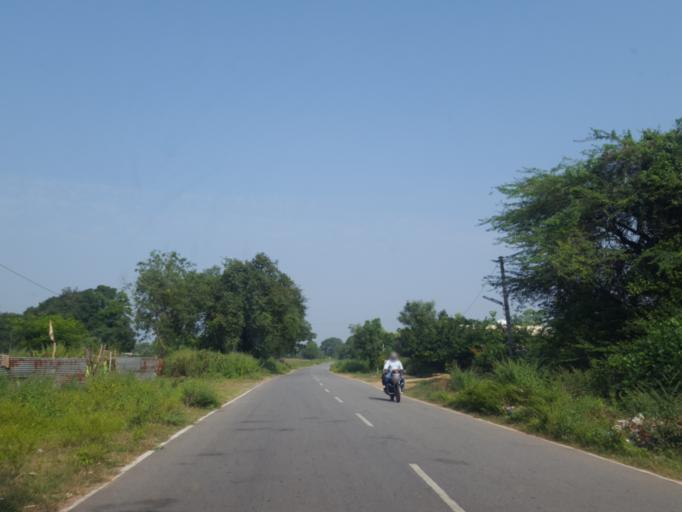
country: IN
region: Telangana
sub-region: Khammam
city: Yellandu
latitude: 17.6197
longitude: 80.3082
